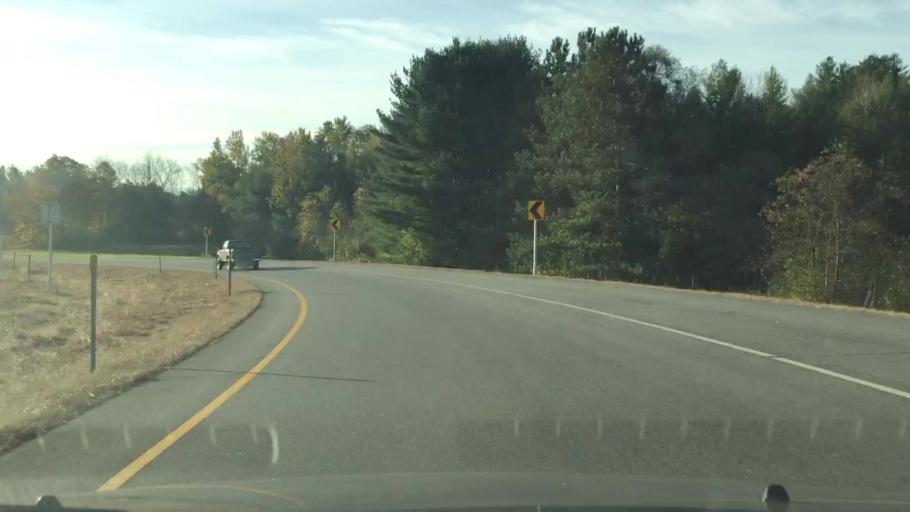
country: US
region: New Hampshire
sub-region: Cheshire County
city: Keene
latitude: 42.9426
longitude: -72.2975
